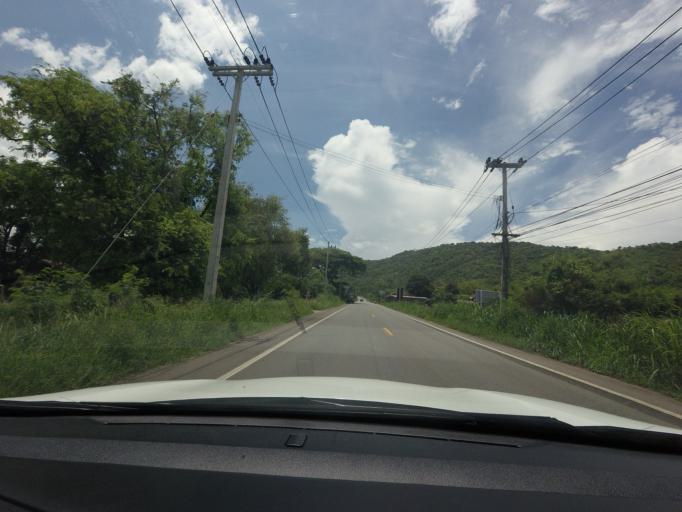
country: TH
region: Sara Buri
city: Muak Lek
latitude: 14.6162
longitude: 101.2122
